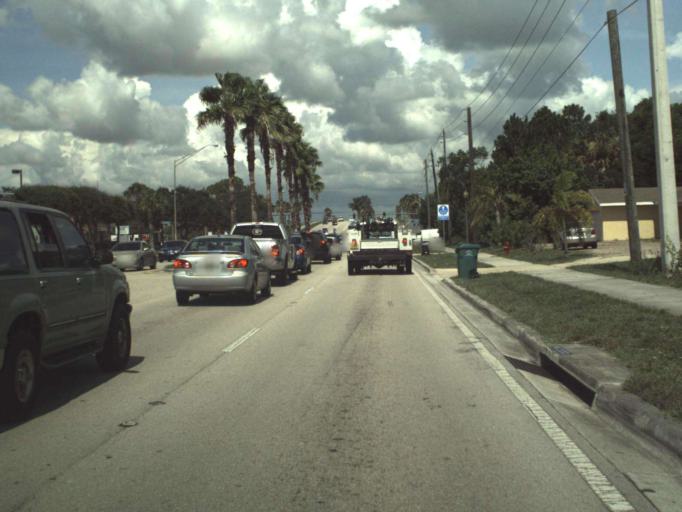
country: US
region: Florida
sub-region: Saint Lucie County
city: River Park
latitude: 27.3179
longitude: -80.3693
